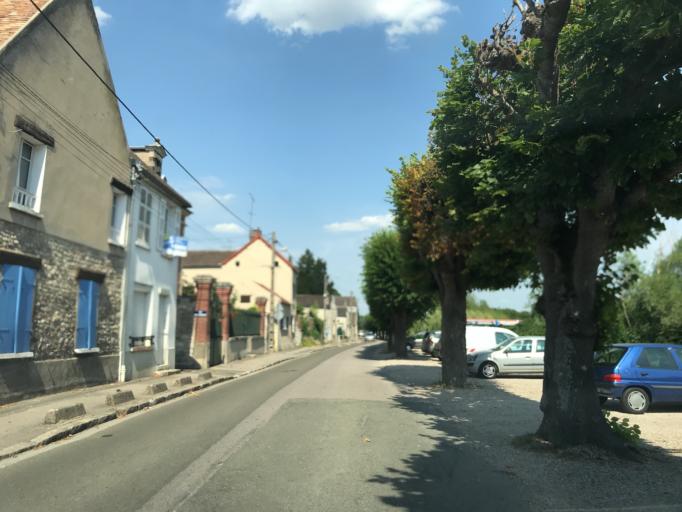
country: FR
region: Ile-de-France
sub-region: Departement des Yvelines
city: Bonnieres-sur-Seine
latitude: 49.0417
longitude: 1.5723
